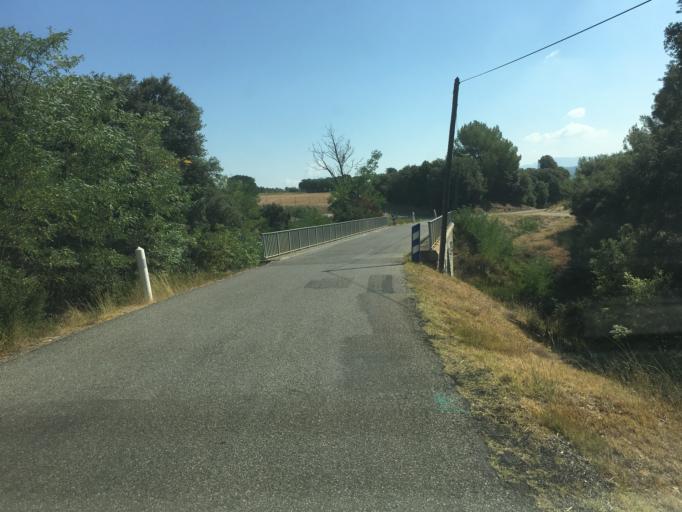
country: FR
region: Provence-Alpes-Cote d'Azur
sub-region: Departement des Alpes-de-Haute-Provence
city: Valensole
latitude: 43.8948
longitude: 5.9969
